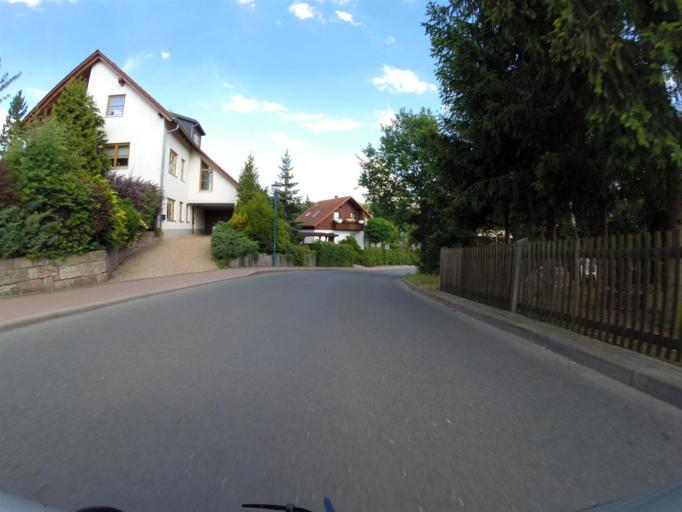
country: DE
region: Thuringia
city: Stadtroda
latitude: 50.8642
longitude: 11.7308
